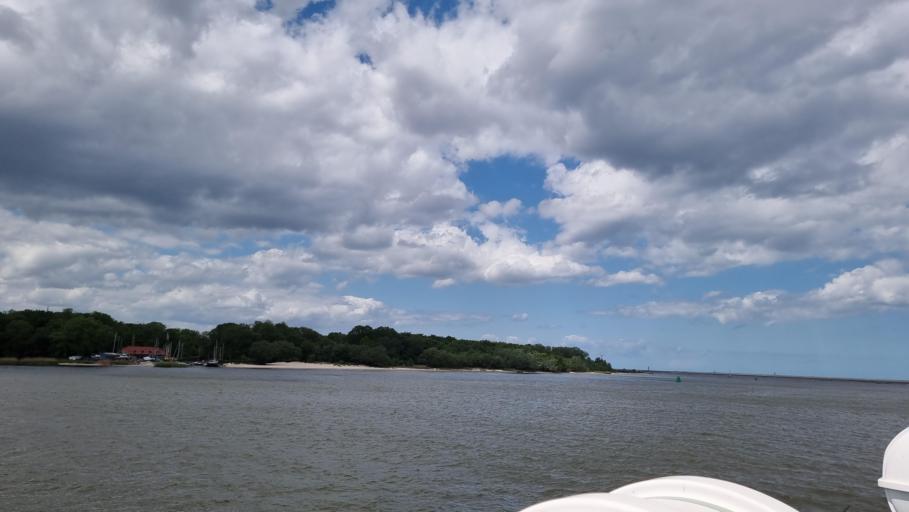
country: PL
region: West Pomeranian Voivodeship
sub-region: Swinoujscie
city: Swinoujscie
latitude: 53.9146
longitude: 14.2808
